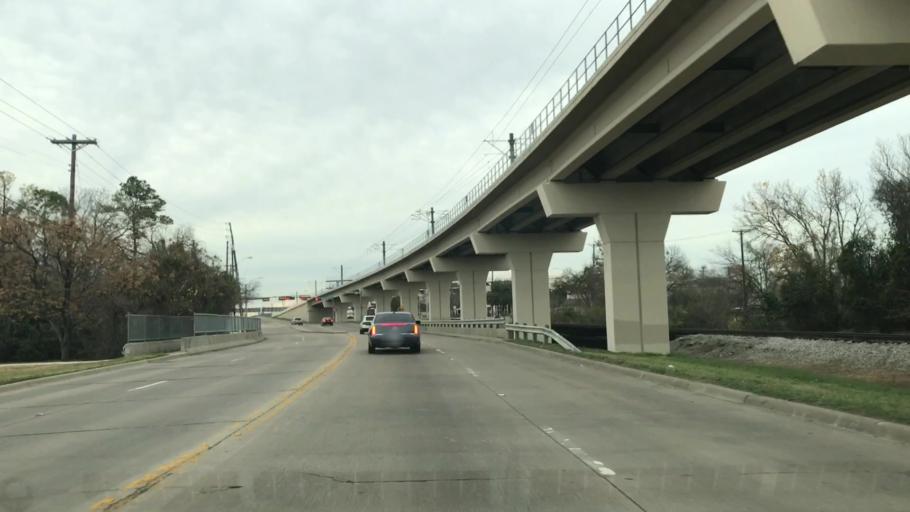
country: US
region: Texas
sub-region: Dallas County
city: University Park
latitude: 32.8465
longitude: -96.8708
